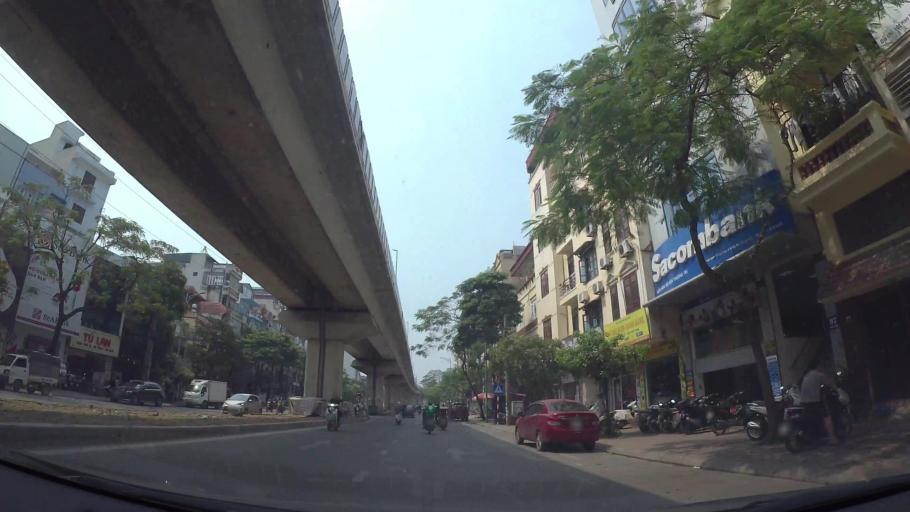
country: VN
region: Ha Noi
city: Dong Da
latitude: 21.0246
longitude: 105.8270
